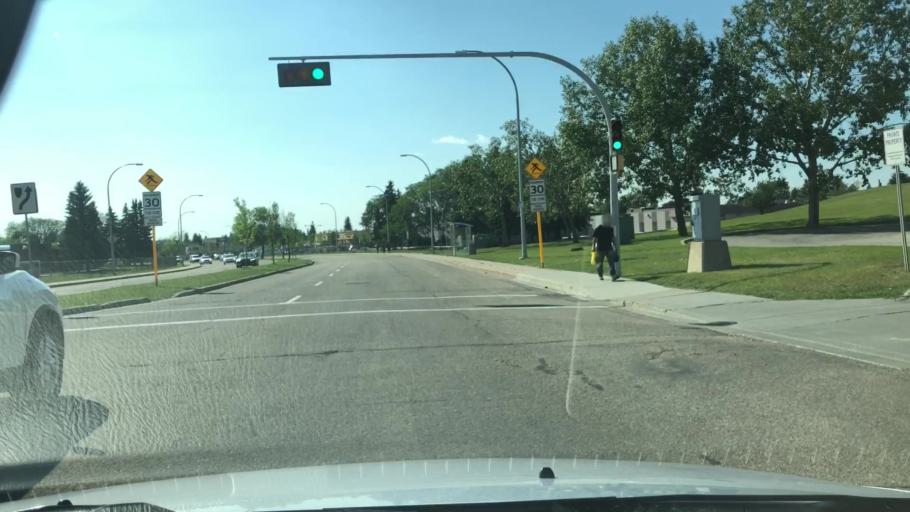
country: CA
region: Alberta
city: Edmonton
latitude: 53.6066
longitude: -113.4540
